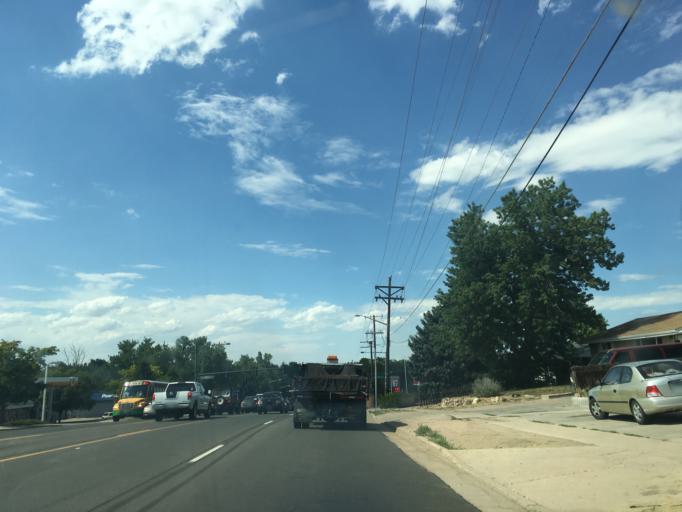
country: US
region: Colorado
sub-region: Jefferson County
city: Lakewood
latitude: 39.6812
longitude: -105.0532
